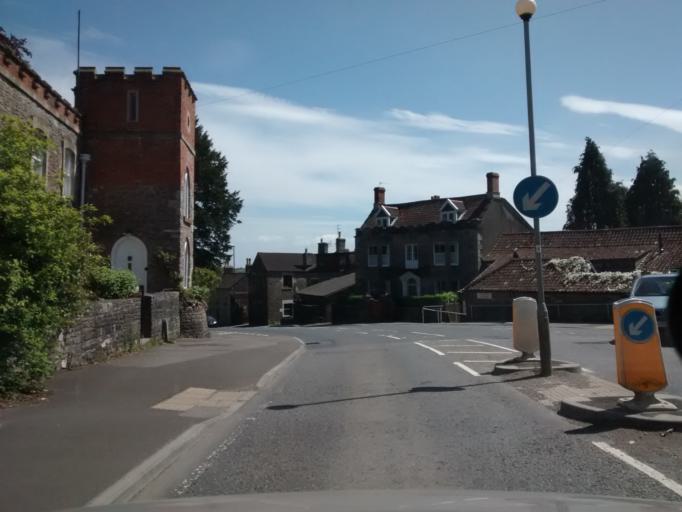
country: GB
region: England
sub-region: Bath and North East Somerset
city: Clutton
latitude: 51.3174
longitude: -2.5423
